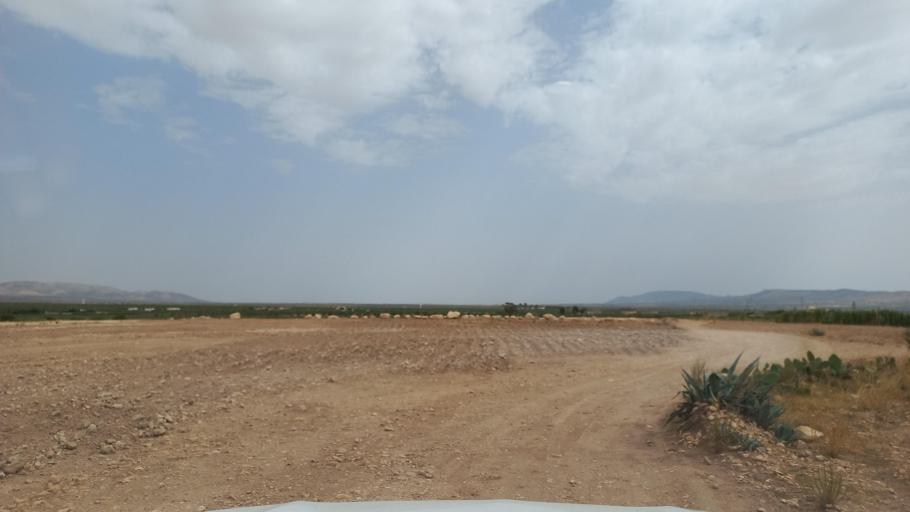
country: TN
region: Al Qasrayn
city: Kasserine
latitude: 35.2802
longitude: 9.0162
